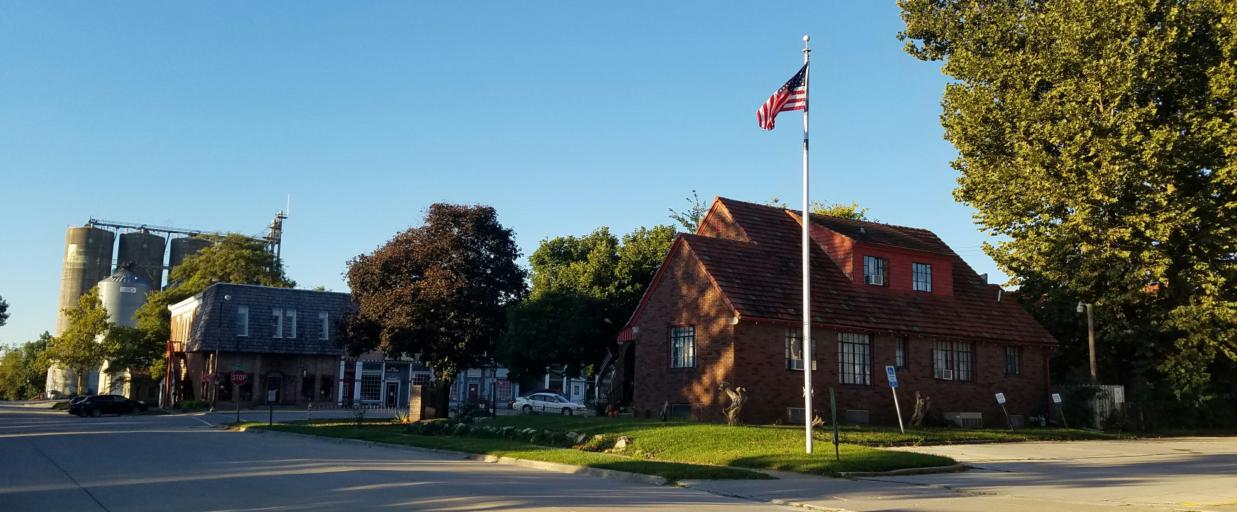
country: US
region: Iowa
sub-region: Decatur County
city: Lamoni
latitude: 40.6244
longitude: -93.9321
